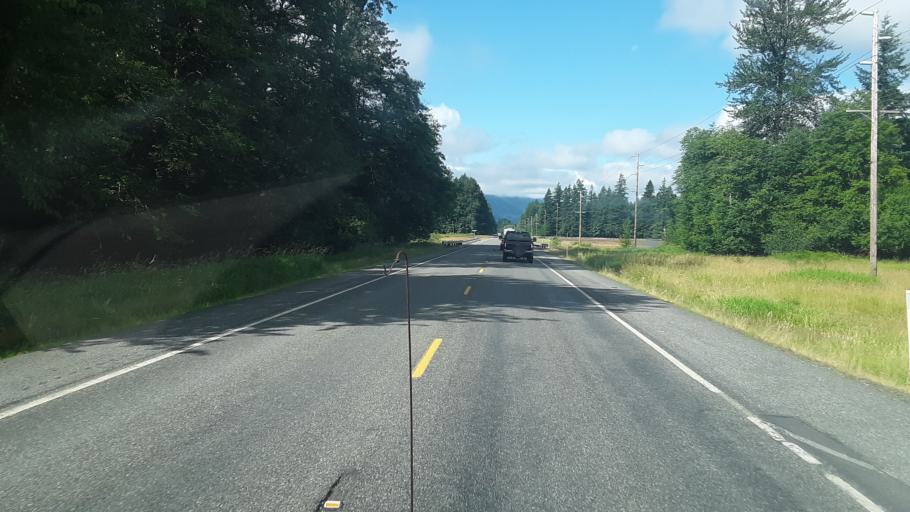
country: US
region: Washington
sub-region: Lewis County
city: Morton
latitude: 46.5591
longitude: -121.7232
